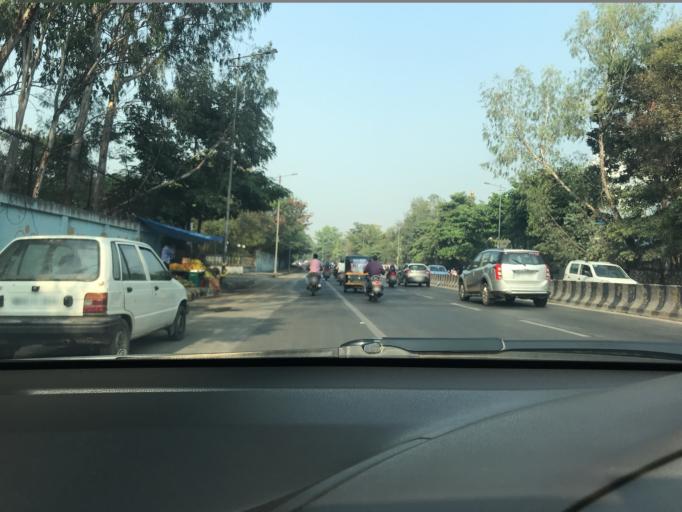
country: IN
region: Maharashtra
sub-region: Pune Division
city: Khadki
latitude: 18.5483
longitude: 73.8139
